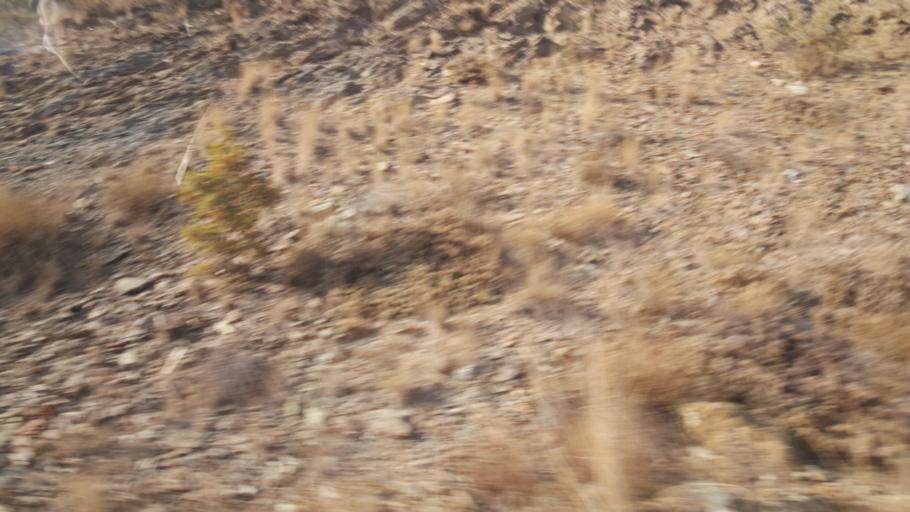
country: TR
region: Eskisehir
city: Kirka
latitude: 39.3347
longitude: 30.5798
